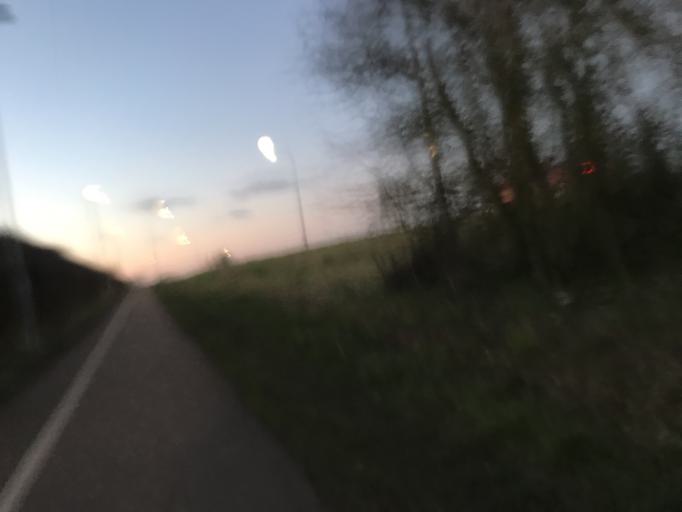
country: GB
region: England
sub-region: North East Lincolnshire
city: Waltham
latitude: 53.5259
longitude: -0.0795
